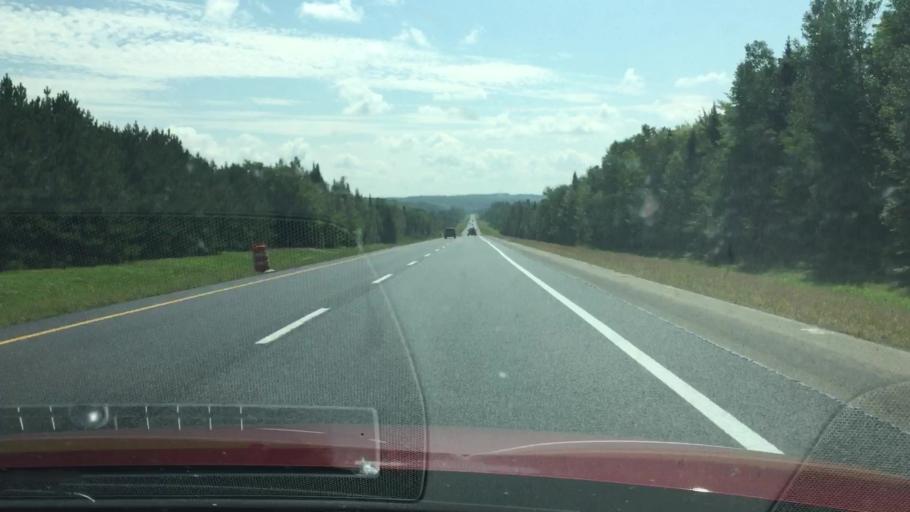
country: US
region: Maine
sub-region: Penobscot County
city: Patten
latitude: 45.8307
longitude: -68.4330
